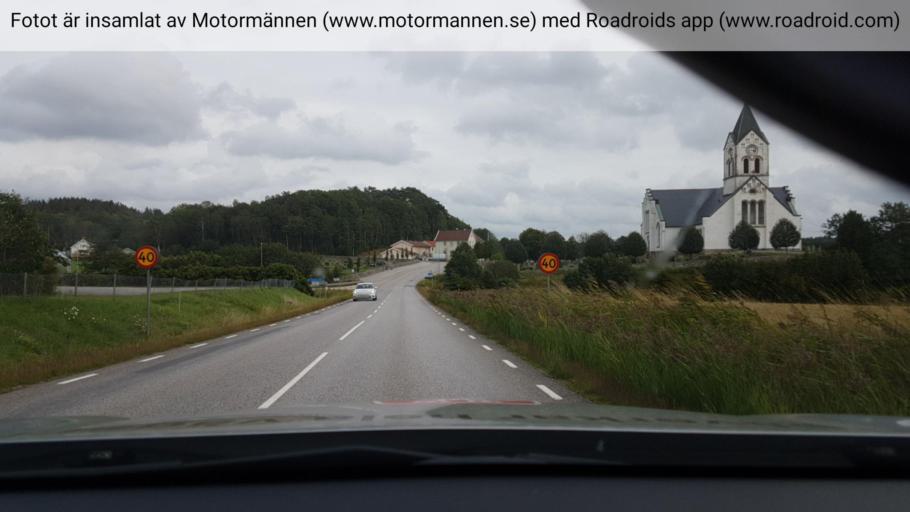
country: SE
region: Vaestra Goetaland
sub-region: Sotenas Kommun
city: Hunnebostrand
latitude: 58.5681
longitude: 11.3646
